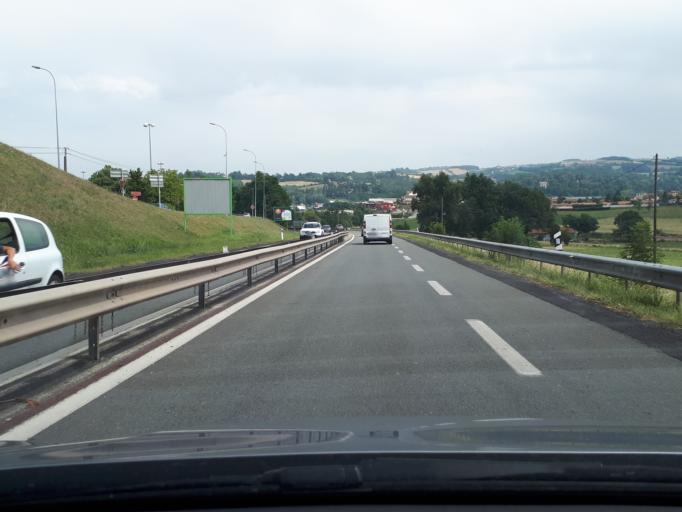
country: FR
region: Rhone-Alpes
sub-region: Departement de la Loire
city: Villars
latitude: 45.4700
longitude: 4.3449
